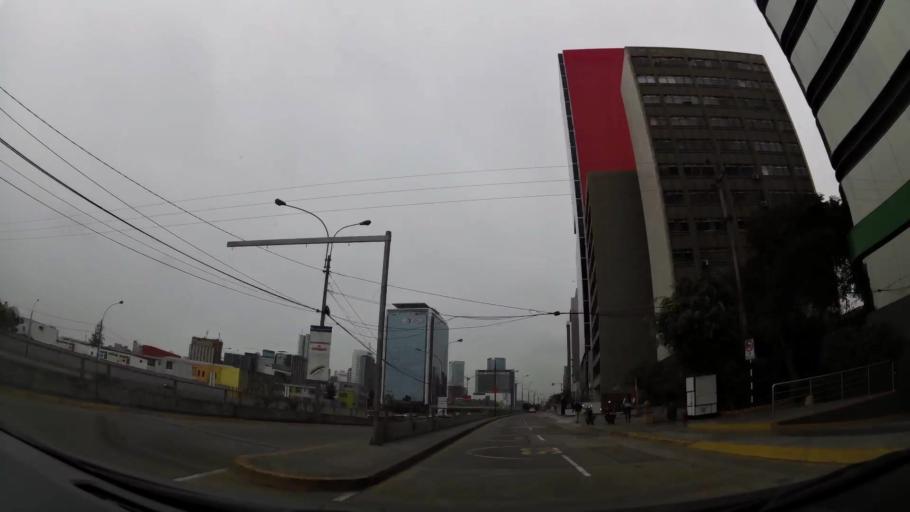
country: PE
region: Lima
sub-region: Lima
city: San Isidro
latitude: -12.1011
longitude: -77.0266
